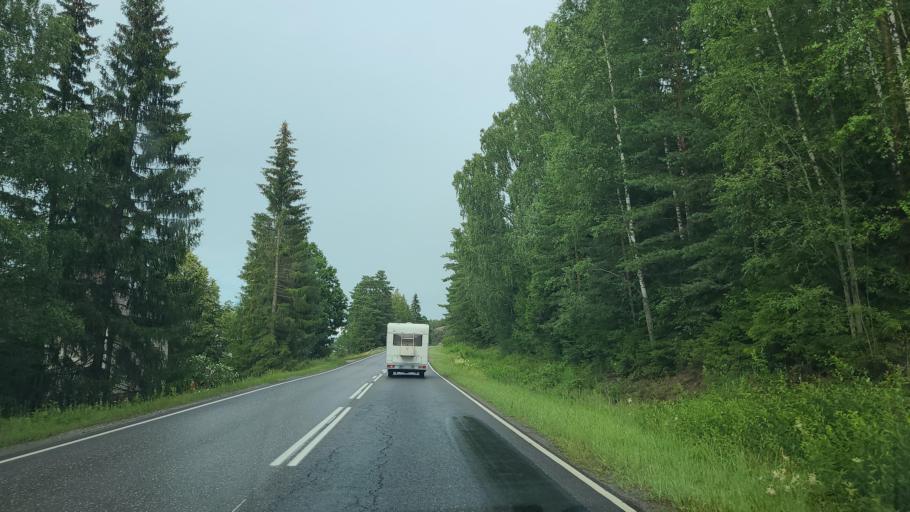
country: FI
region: Varsinais-Suomi
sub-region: Turku
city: Sauvo
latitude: 60.3129
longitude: 22.6909
